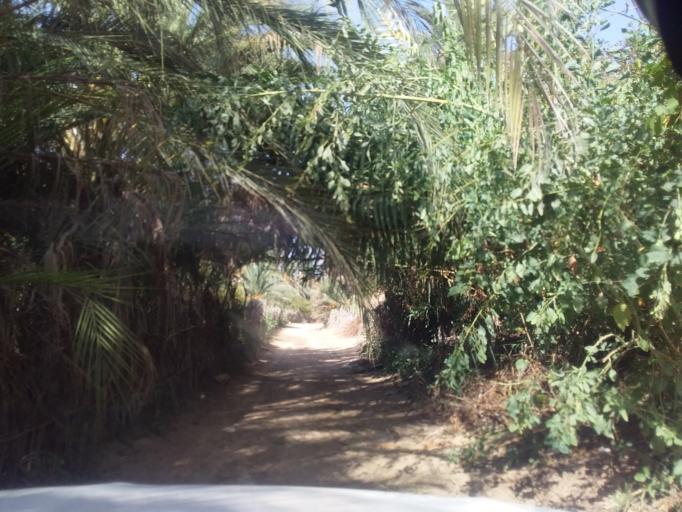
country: TN
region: Qabis
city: Gabes
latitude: 33.6250
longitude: 10.2846
